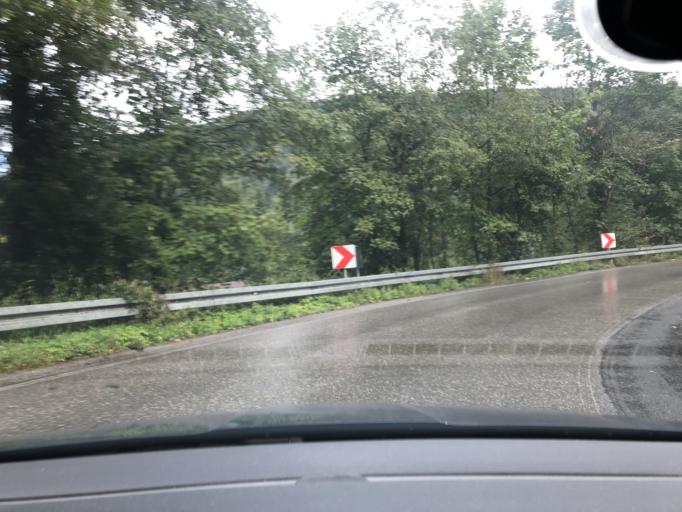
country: PL
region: Lesser Poland Voivodeship
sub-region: Powiat suski
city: Stryszawa
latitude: 49.6921
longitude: 19.5507
